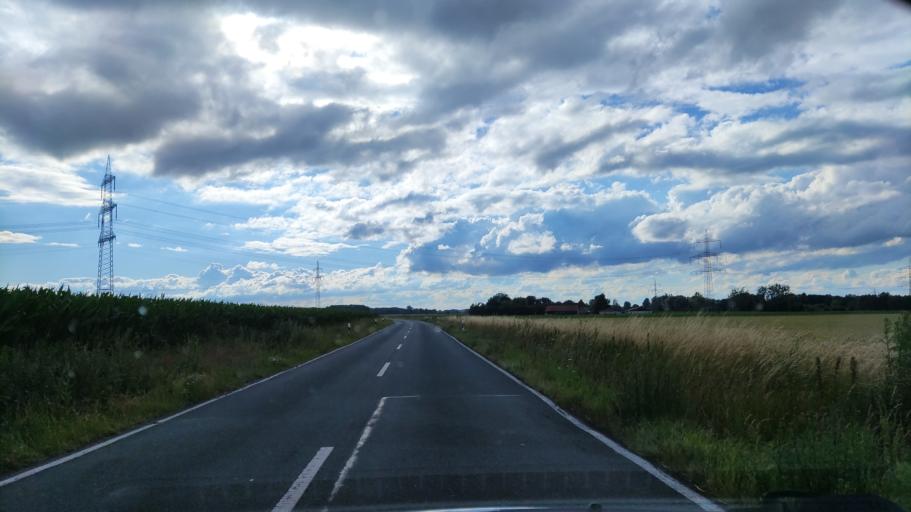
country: DE
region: North Rhine-Westphalia
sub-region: Regierungsbezirk Arnsberg
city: Welver
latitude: 51.6256
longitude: 8.0175
